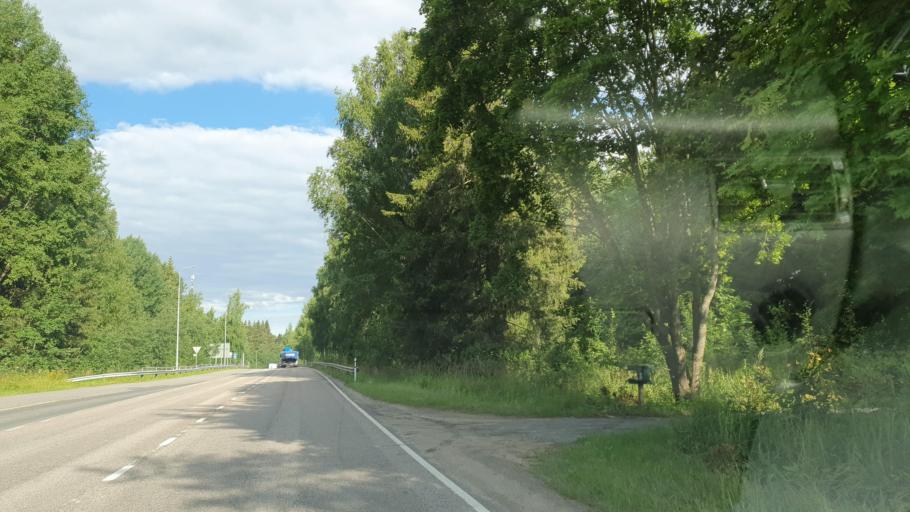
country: FI
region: Central Finland
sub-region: Jyvaeskylae
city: Saeynaetsalo
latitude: 62.1802
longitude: 25.7295
